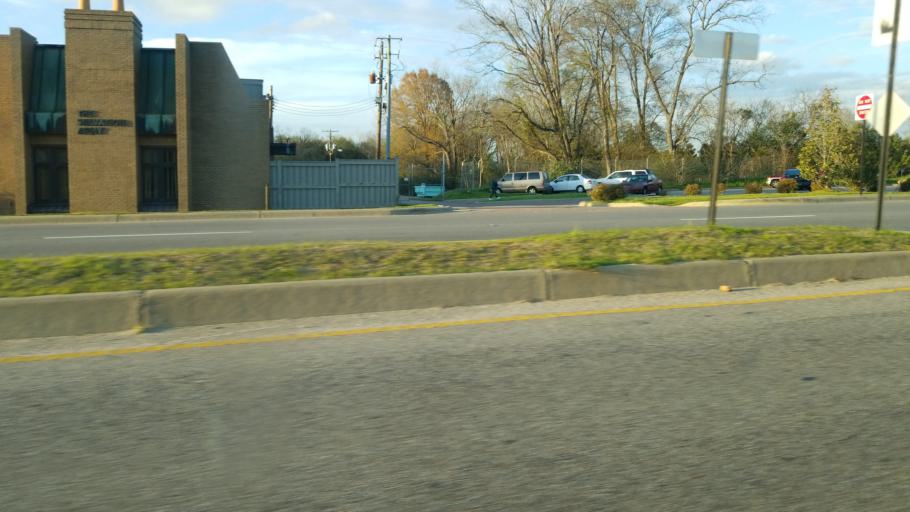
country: US
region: Alabama
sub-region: Montgomery County
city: Montgomery
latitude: 32.3775
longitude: -86.3264
